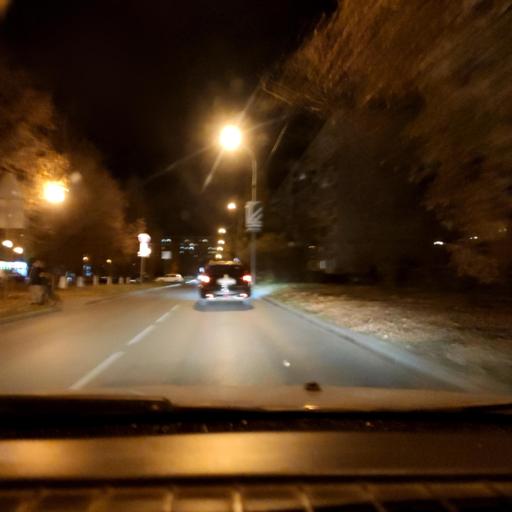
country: RU
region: Samara
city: Tol'yatti
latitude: 53.5370
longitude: 49.3213
